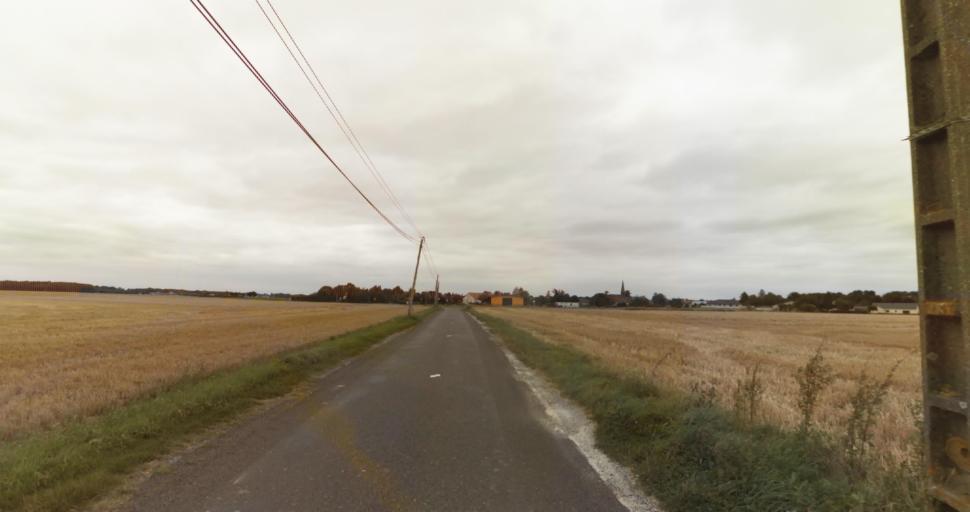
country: FR
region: Haute-Normandie
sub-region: Departement de l'Eure
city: Menilles
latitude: 48.9514
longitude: 1.2647
